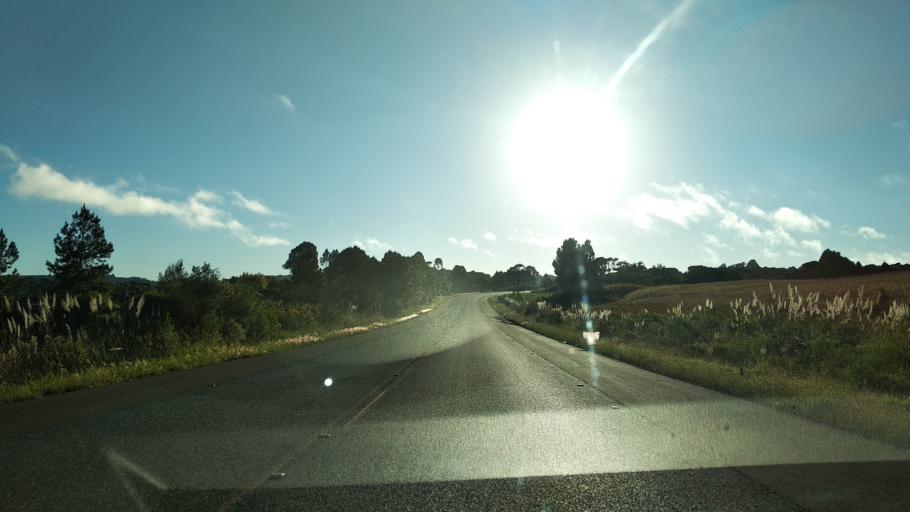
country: BR
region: Santa Catarina
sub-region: Correia Pinto
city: Correia Pinto
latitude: -27.6231
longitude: -50.6484
